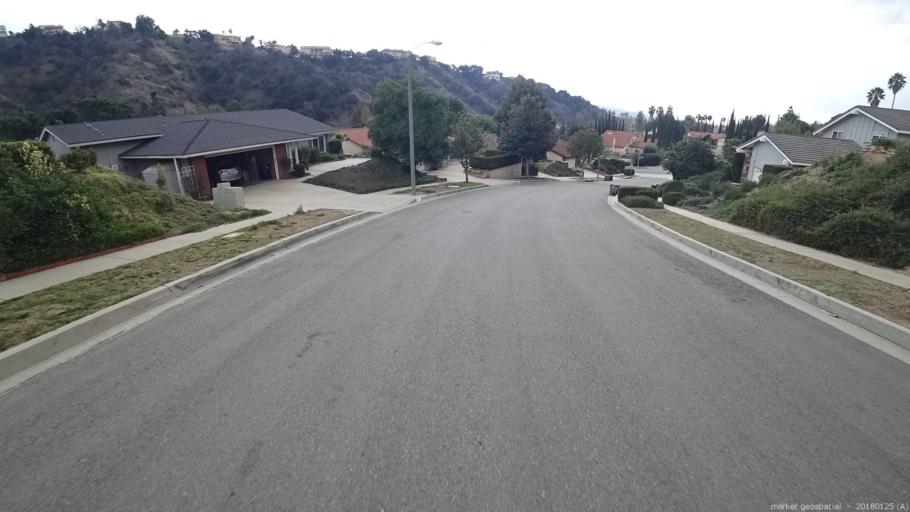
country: US
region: California
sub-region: Los Angeles County
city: Diamond Bar
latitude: 33.9881
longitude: -117.8245
